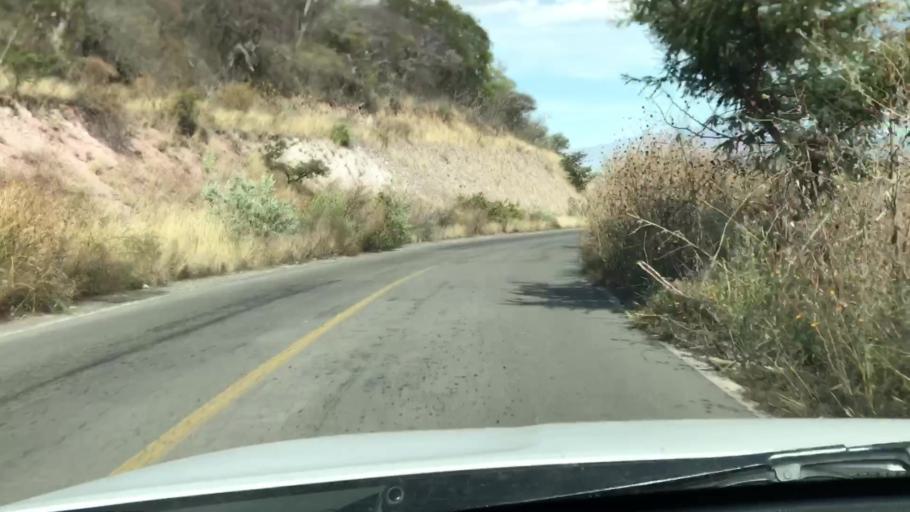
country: MX
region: Jalisco
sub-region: Zacoalco de Torres
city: Barranca de Otates (Barranca de Otatan)
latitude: 20.2451
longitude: -103.6682
